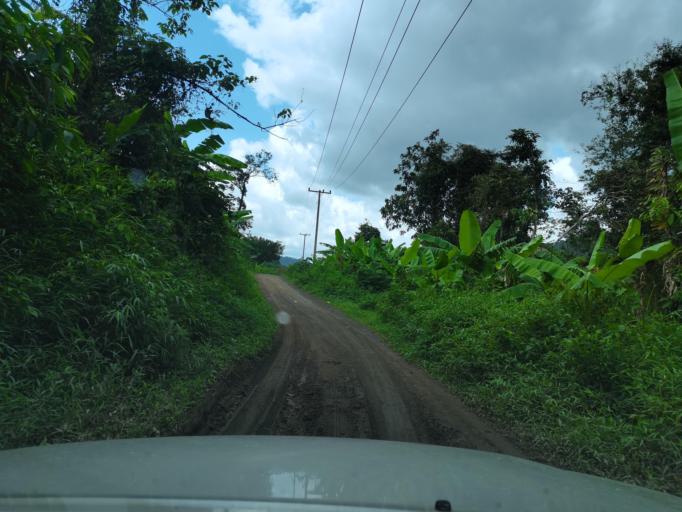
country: LA
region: Loungnamtha
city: Muang Long
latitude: 20.7736
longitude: 101.0166
